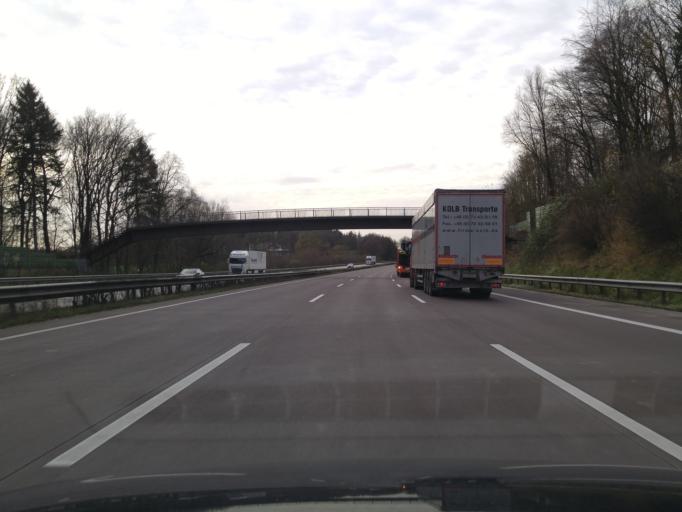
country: DE
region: Schleswig-Holstein
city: Grosshansdorf
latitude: 53.6551
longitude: 10.2952
